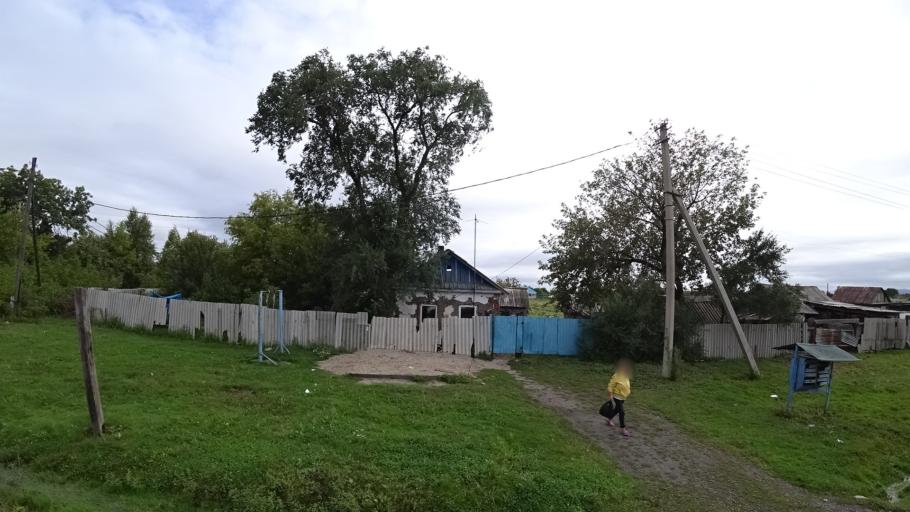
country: RU
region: Primorskiy
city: Chernigovka
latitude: 44.3447
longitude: 132.5604
